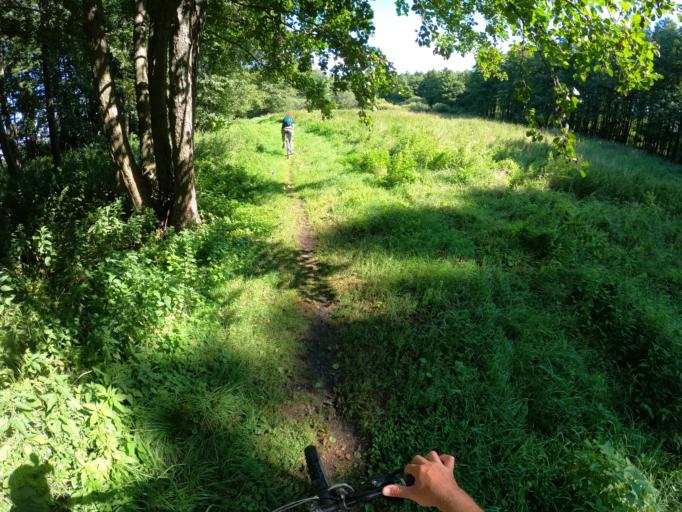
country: LT
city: Neringa
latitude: 55.3977
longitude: 21.2350
